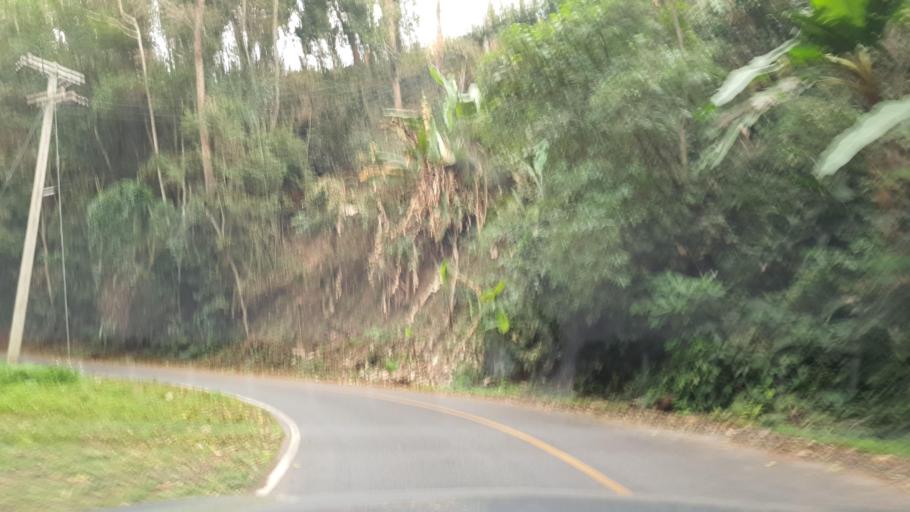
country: TH
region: Chiang Mai
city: Mae On
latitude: 18.9404
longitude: 99.3658
